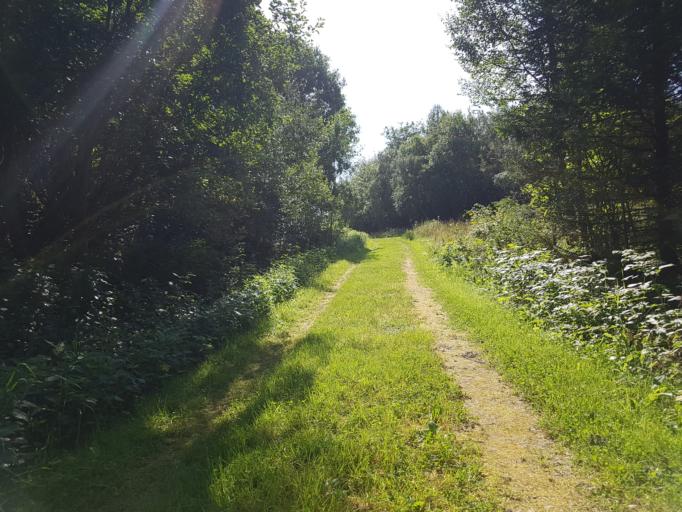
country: NO
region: Sor-Trondelag
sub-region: Agdenes
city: Lensvik
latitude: 63.6340
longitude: 9.8413
